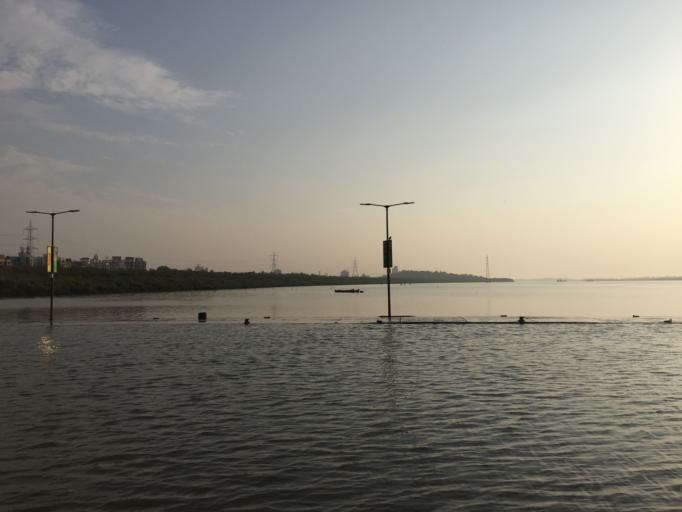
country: IN
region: Maharashtra
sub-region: Mumbai Suburban
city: Borivli
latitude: 19.2347
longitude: 72.8223
